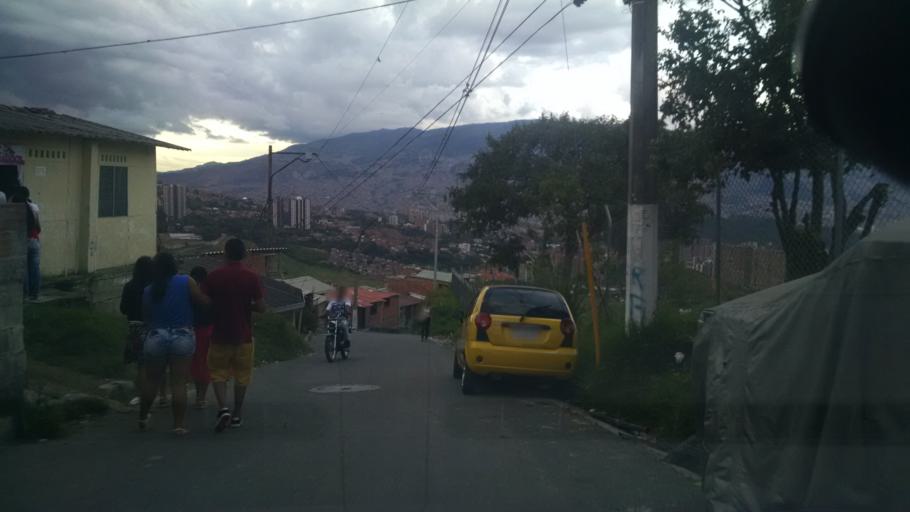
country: CO
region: Antioquia
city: Medellin
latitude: 6.2725
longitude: -75.6108
